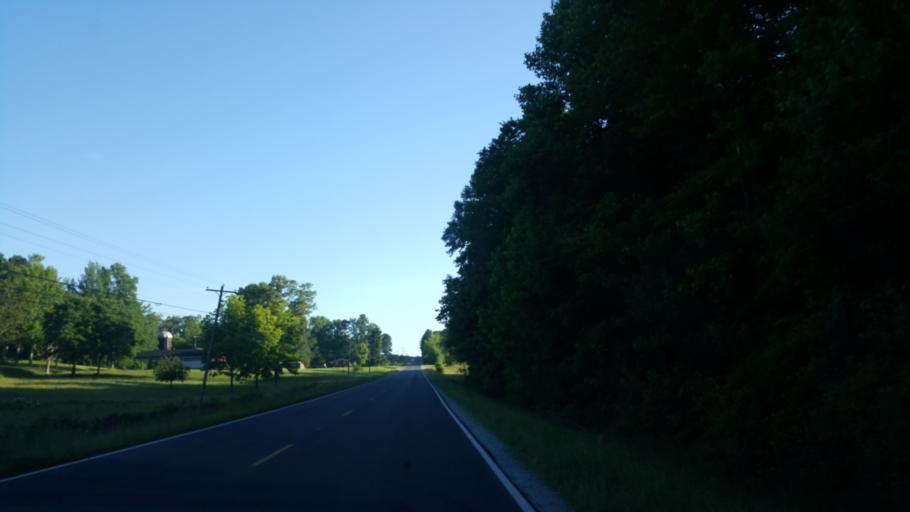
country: US
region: Tennessee
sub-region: Henderson County
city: Lexington
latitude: 35.5554
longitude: -88.3855
